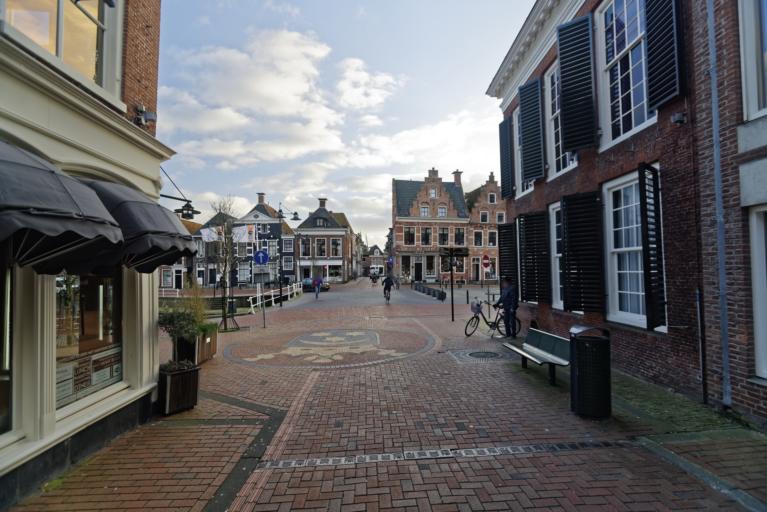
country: NL
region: Friesland
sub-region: Gemeente Dongeradeel
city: Dokkum
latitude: 53.3253
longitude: 5.9981
